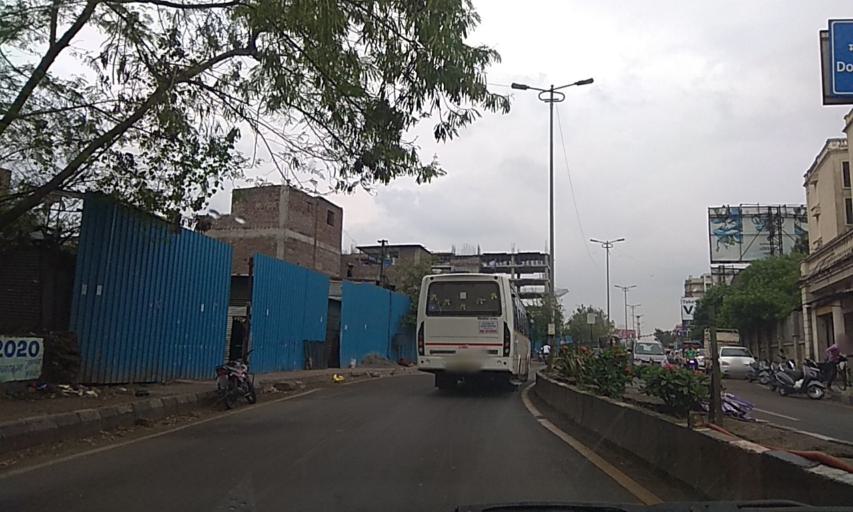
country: IN
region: Maharashtra
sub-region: Pune Division
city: Lohogaon
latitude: 18.5666
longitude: 73.9066
